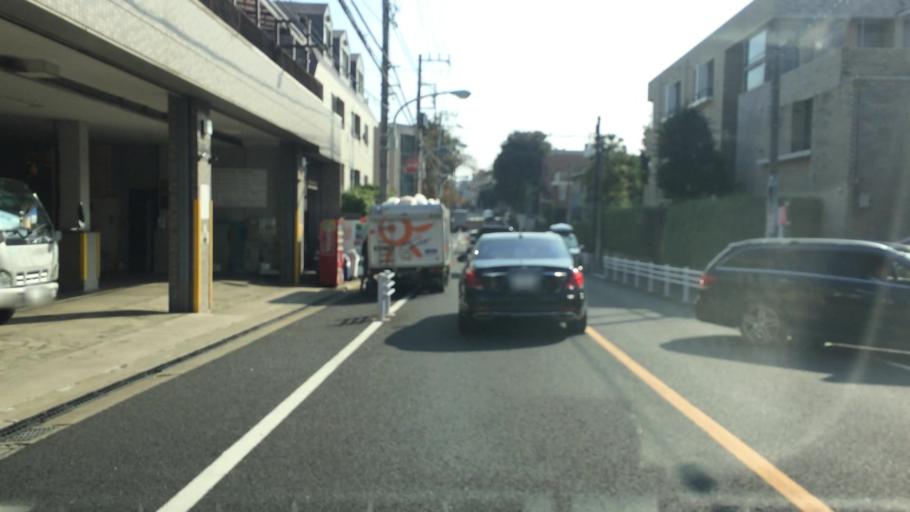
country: JP
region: Tokyo
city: Tokyo
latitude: 35.6219
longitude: 139.6667
